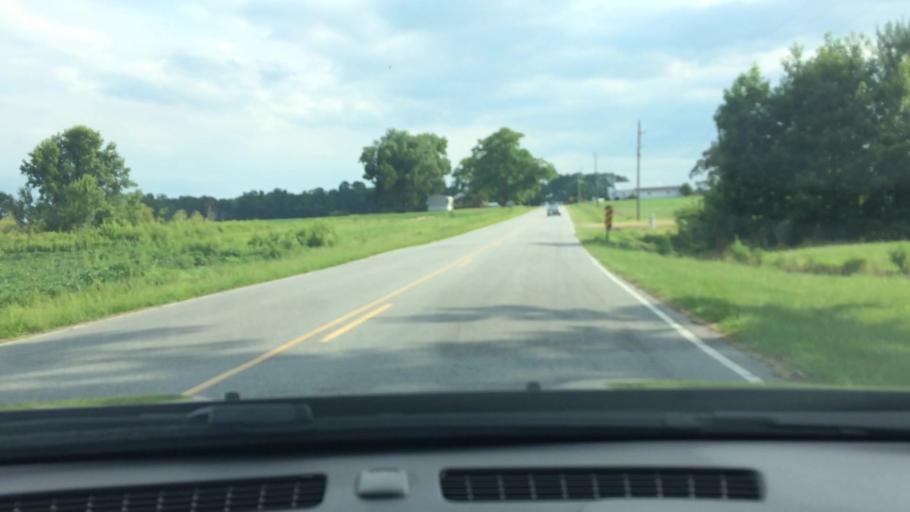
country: US
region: North Carolina
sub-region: Pitt County
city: Ayden
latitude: 35.4874
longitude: -77.3736
